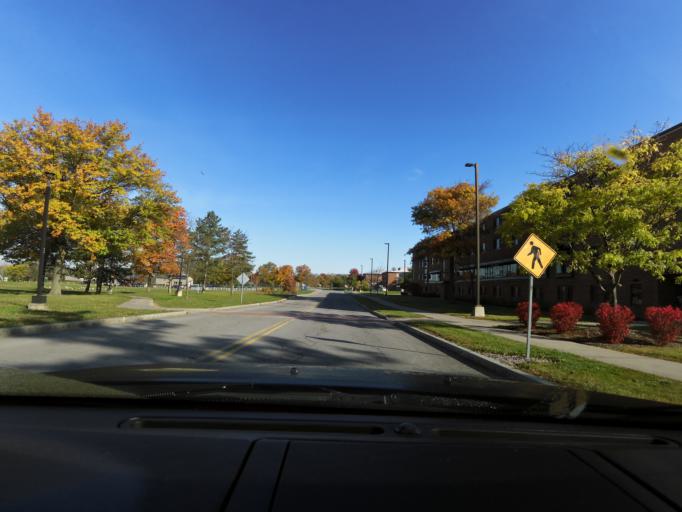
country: US
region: New York
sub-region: Livingston County
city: Geneseo
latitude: 42.7978
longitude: -77.8235
